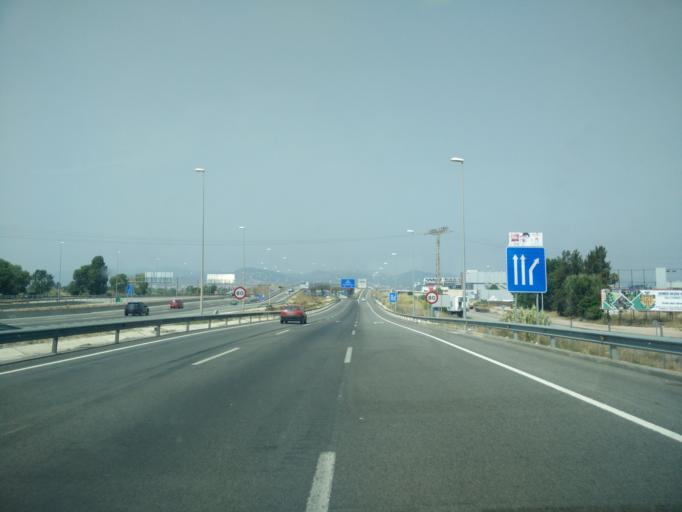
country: ES
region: Catalonia
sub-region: Provincia de Barcelona
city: Cornella de Llobregat
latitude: 41.3454
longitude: 2.0869
